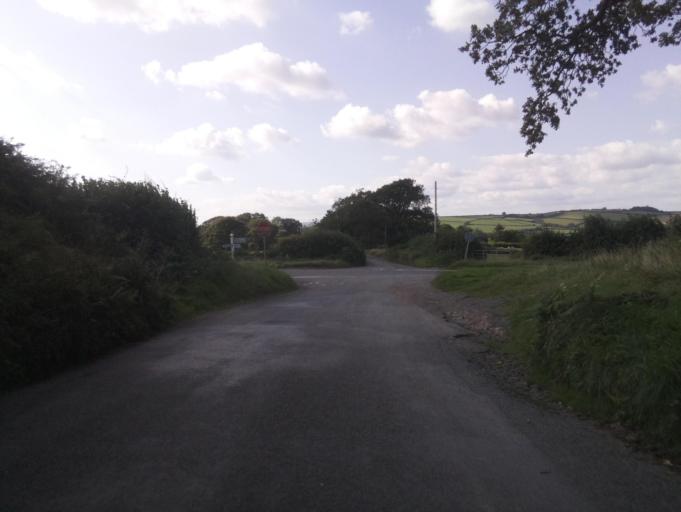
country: GB
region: England
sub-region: Devon
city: Totnes
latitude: 50.4266
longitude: -3.7426
